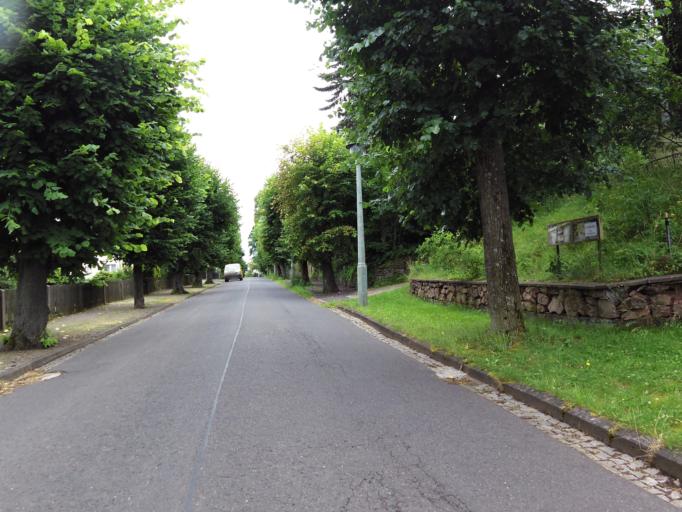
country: DE
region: Thuringia
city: Tabarz
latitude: 50.8749
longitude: 10.5017
